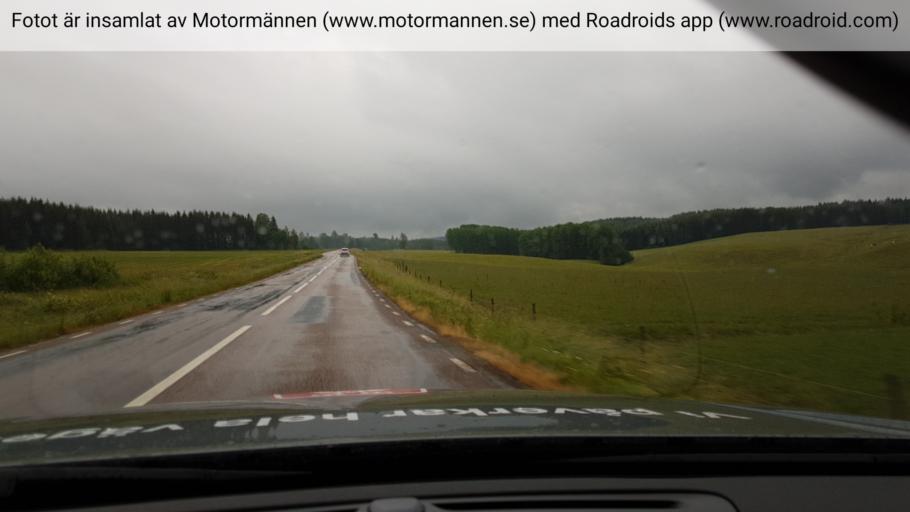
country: SE
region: Dalarna
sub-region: Avesta Kommun
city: Avesta
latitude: 59.9976
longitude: 16.0887
